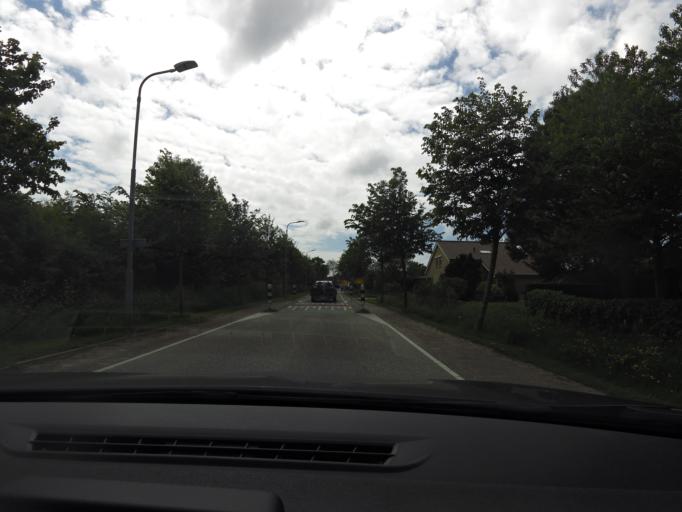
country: NL
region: Zeeland
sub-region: Schouwen-Duiveland
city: Scharendijke
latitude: 51.7309
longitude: 3.8179
